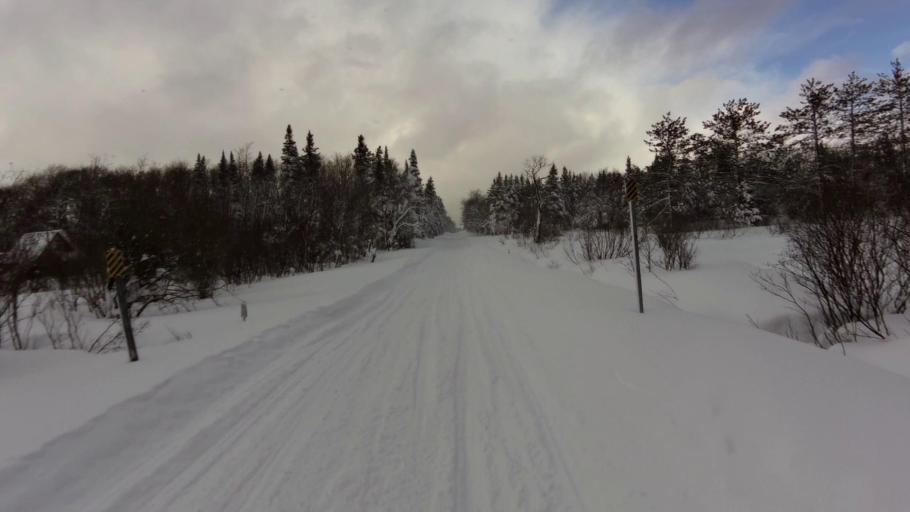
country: US
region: New York
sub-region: Lewis County
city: Lowville
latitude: 43.7363
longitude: -75.6713
